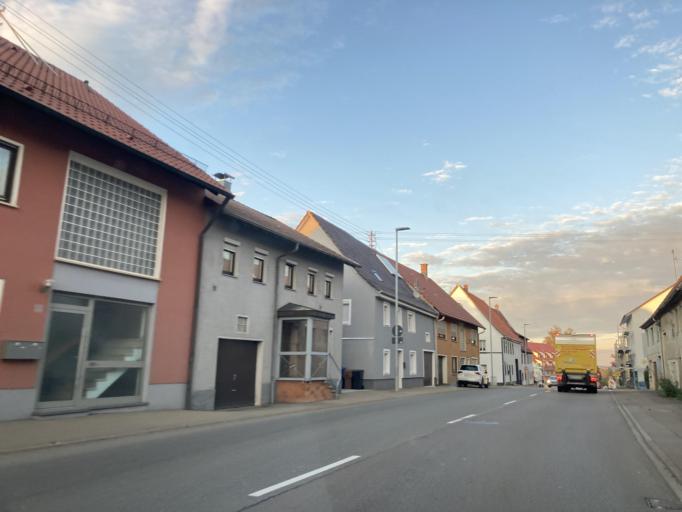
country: DE
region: Baden-Wuerttemberg
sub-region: Tuebingen Region
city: Schomberg
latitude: 48.2103
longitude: 8.7563
